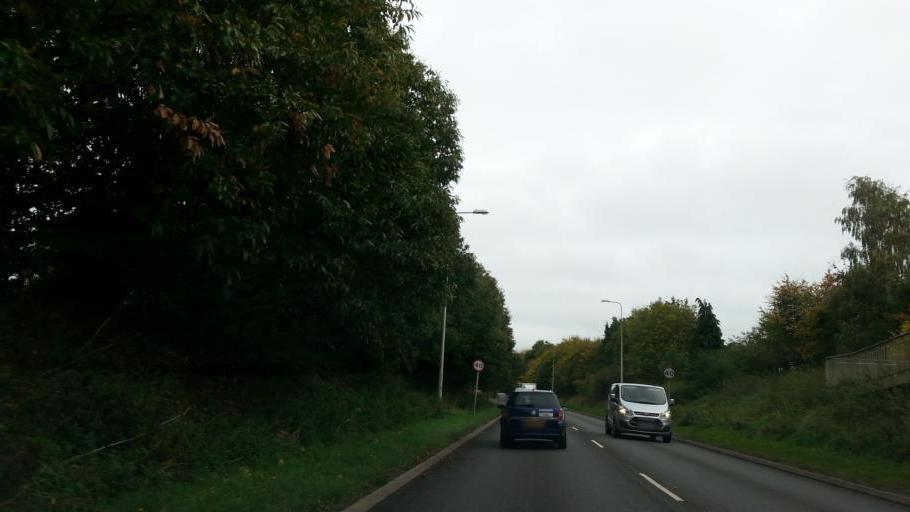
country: GB
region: England
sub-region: Worcestershire
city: Bromsgrove
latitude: 52.3322
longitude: -2.0497
